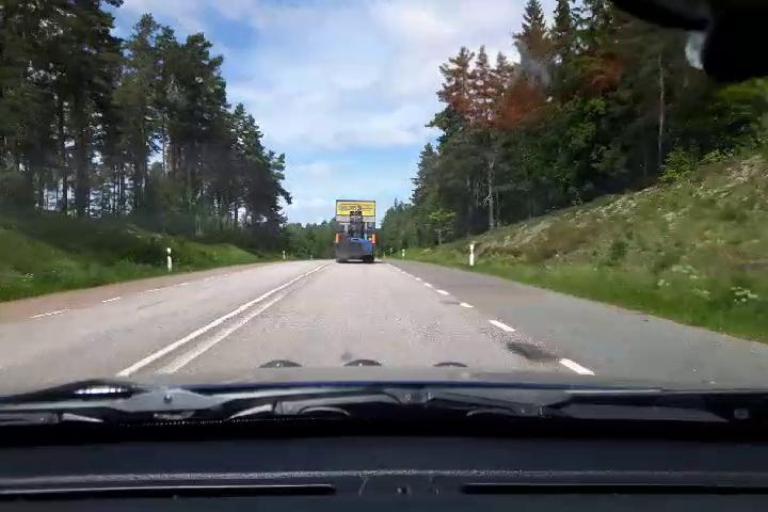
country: SE
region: Uppsala
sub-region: Osthammars Kommun
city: Bjorklinge
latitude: 60.0936
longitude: 17.5544
